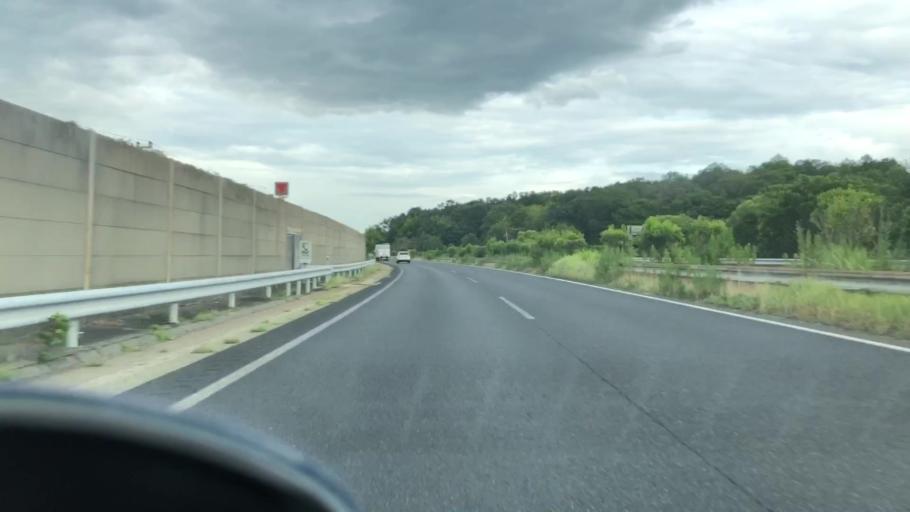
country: JP
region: Hyogo
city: Yashiro
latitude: 34.9183
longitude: 135.0118
